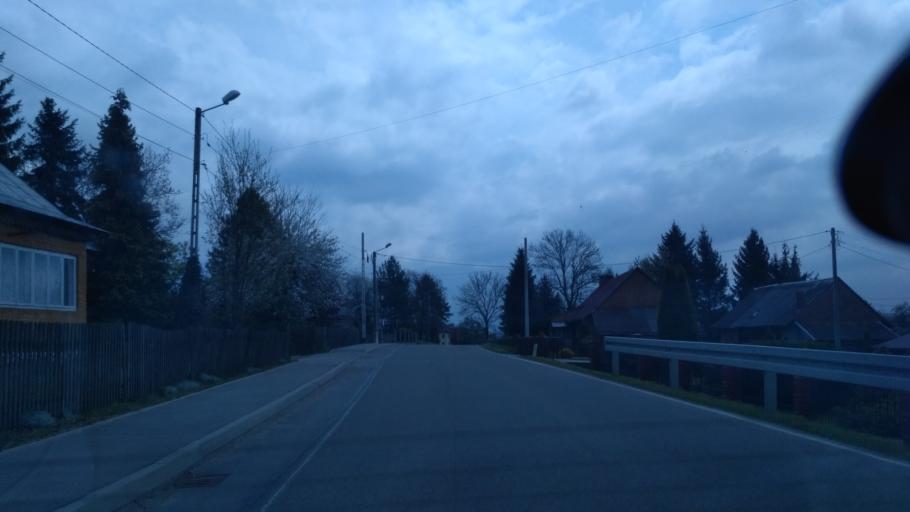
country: PL
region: Subcarpathian Voivodeship
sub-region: Powiat brzozowski
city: Haczow
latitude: 49.6588
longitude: 21.9075
